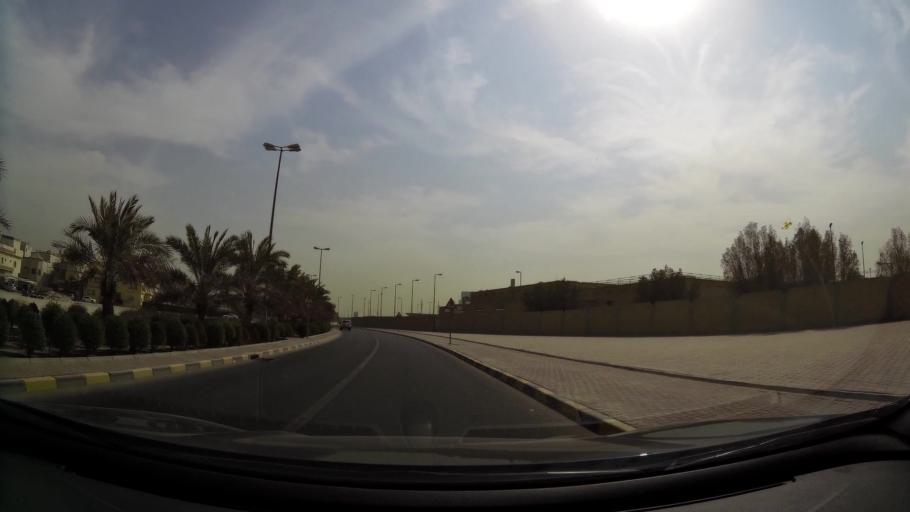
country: KW
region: Al Farwaniyah
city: Janub as Surrah
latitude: 29.2721
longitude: 47.9977
